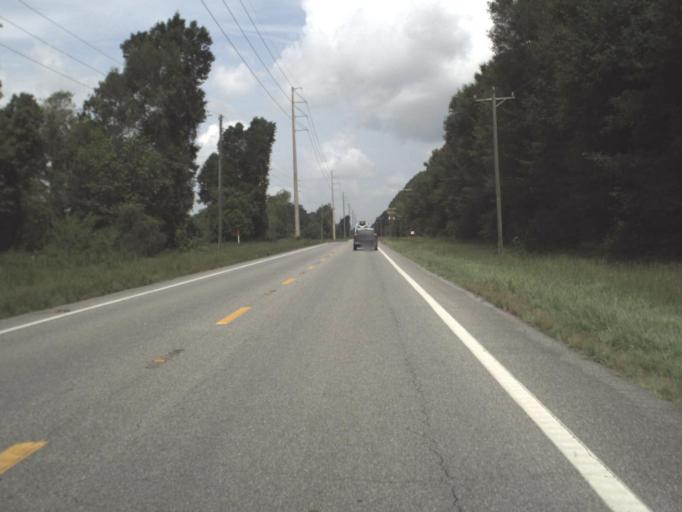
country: US
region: Florida
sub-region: Madison County
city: Madison
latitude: 30.4096
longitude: -83.2592
